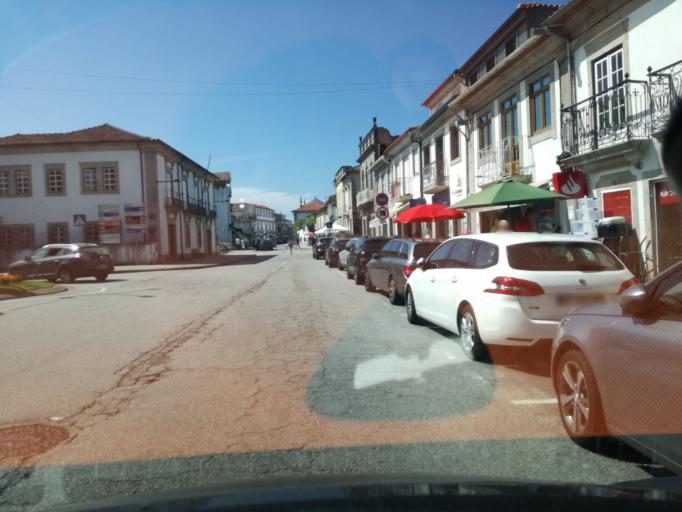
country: ES
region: Galicia
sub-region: Provincia de Pontevedra
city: A Guarda
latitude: 41.8775
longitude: -8.8372
